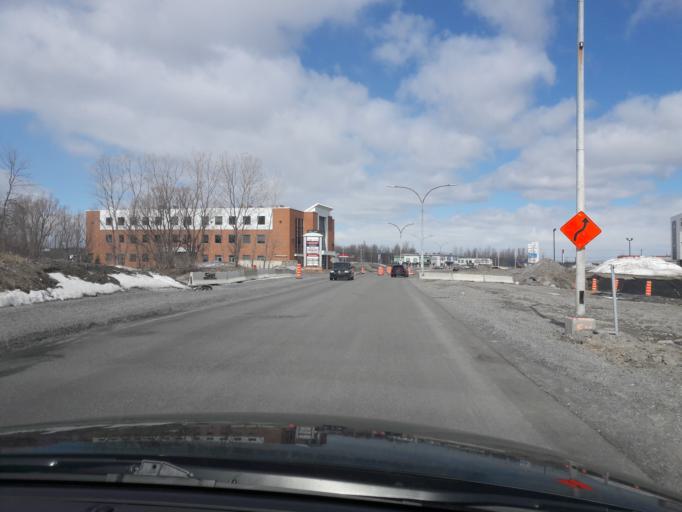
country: CA
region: Quebec
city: Dollard-Des Ormeaux
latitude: 45.5576
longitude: -73.7898
